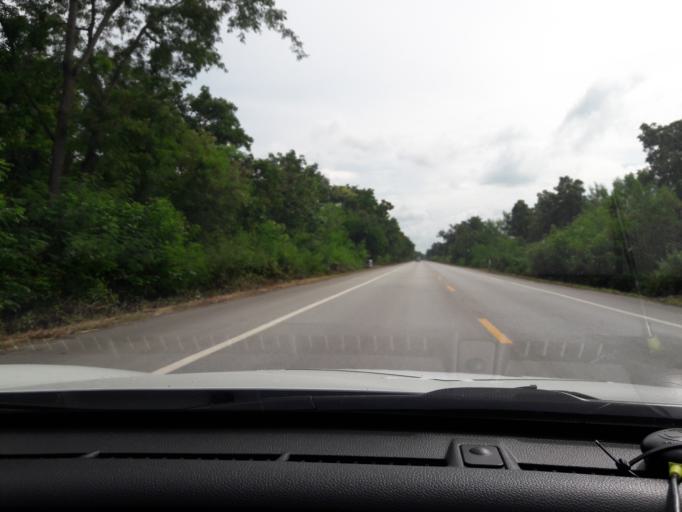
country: TH
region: Nakhon Sawan
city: Tak Fa
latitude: 15.4846
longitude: 100.5364
